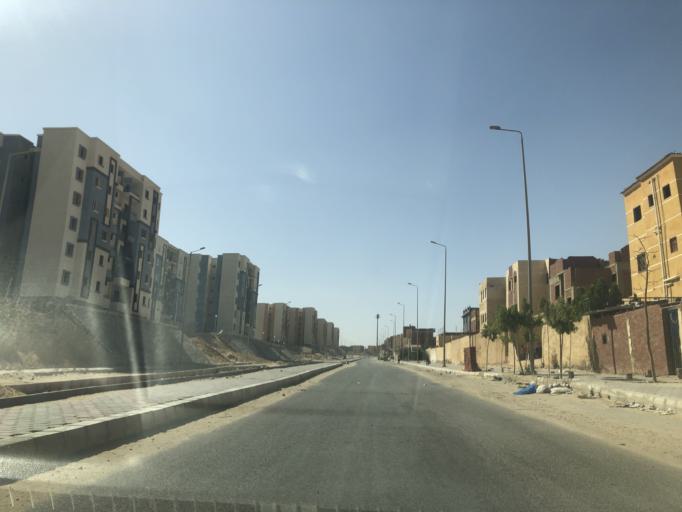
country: EG
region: Al Jizah
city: Madinat Sittah Uktubar
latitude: 29.9328
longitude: 30.9838
